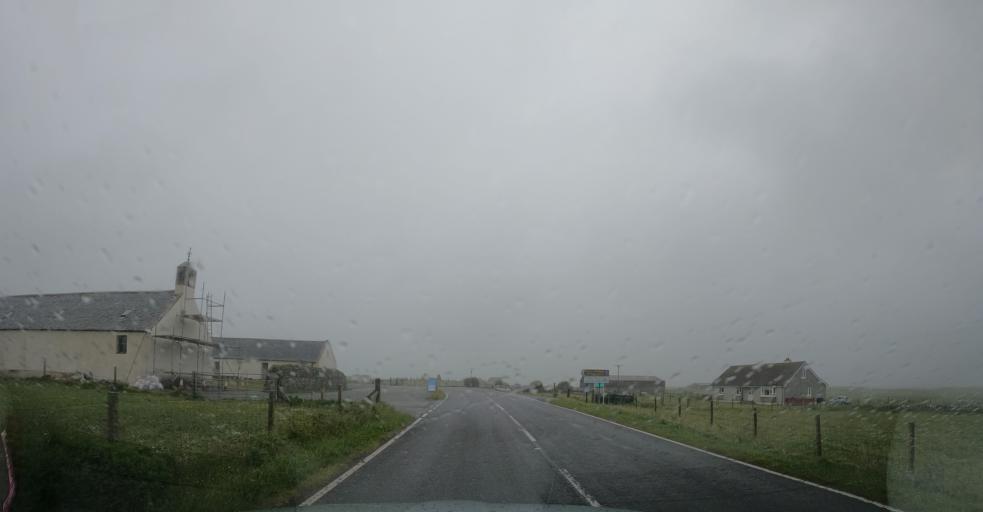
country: GB
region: Scotland
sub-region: Eilean Siar
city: Benbecula
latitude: 57.4573
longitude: -7.3960
